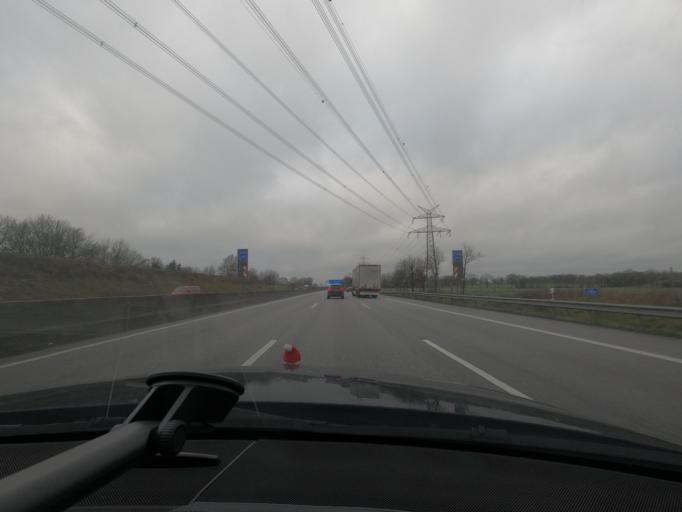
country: DE
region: Schleswig-Holstein
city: Alveslohe
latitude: 53.7931
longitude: 9.9349
